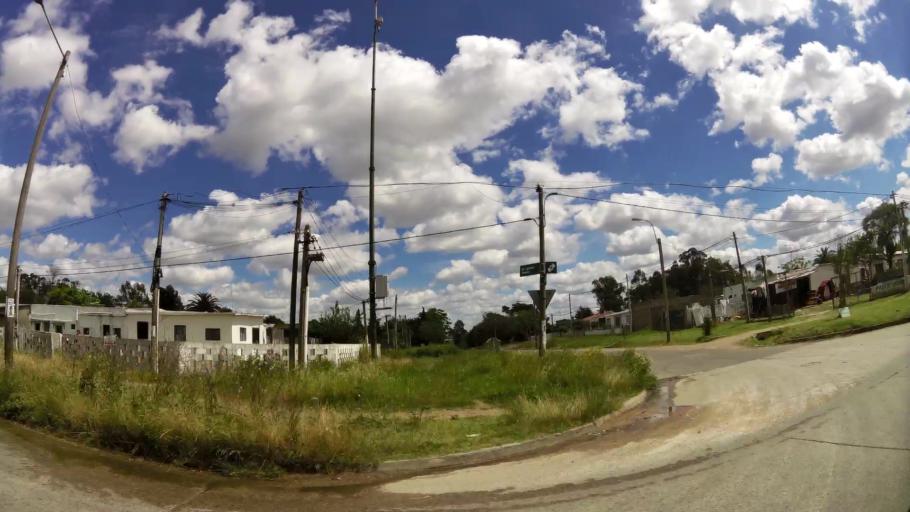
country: UY
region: Canelones
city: Colonia Nicolich
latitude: -34.8242
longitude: -56.1116
